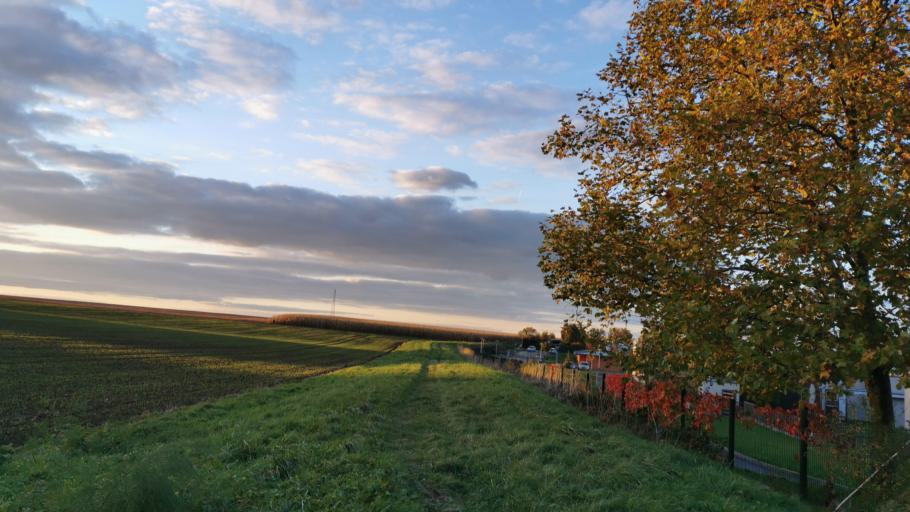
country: FR
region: Ile-de-France
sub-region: Departement des Yvelines
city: Plaisir
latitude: 48.8235
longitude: 1.9361
